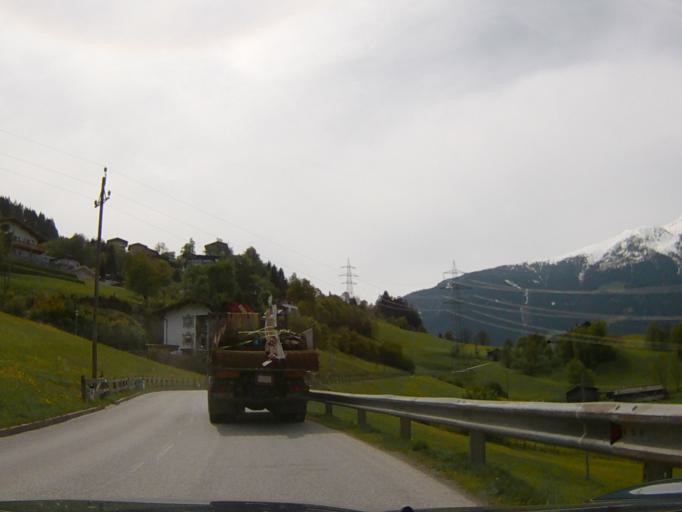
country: AT
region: Tyrol
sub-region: Politischer Bezirk Schwaz
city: Hainzenberg
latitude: 47.2234
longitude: 11.8927
